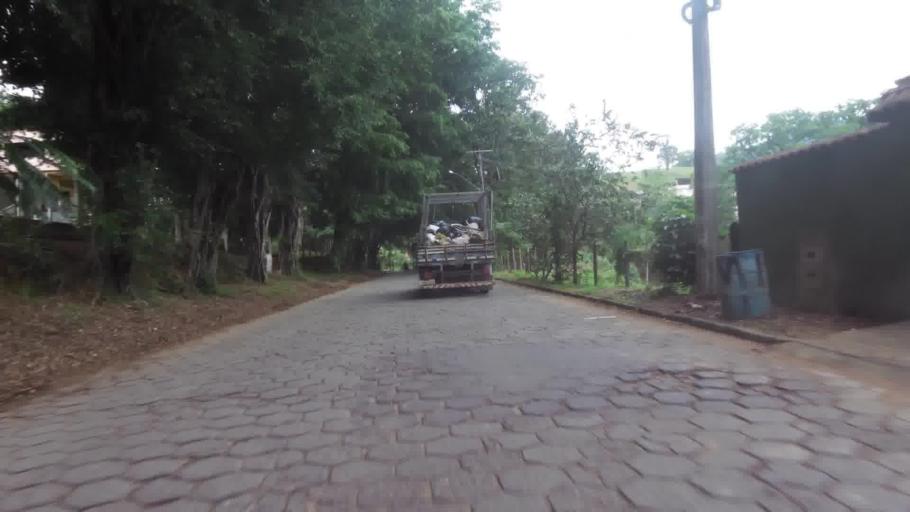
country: BR
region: Espirito Santo
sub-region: Iconha
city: Iconha
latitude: -20.7831
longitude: -40.8255
